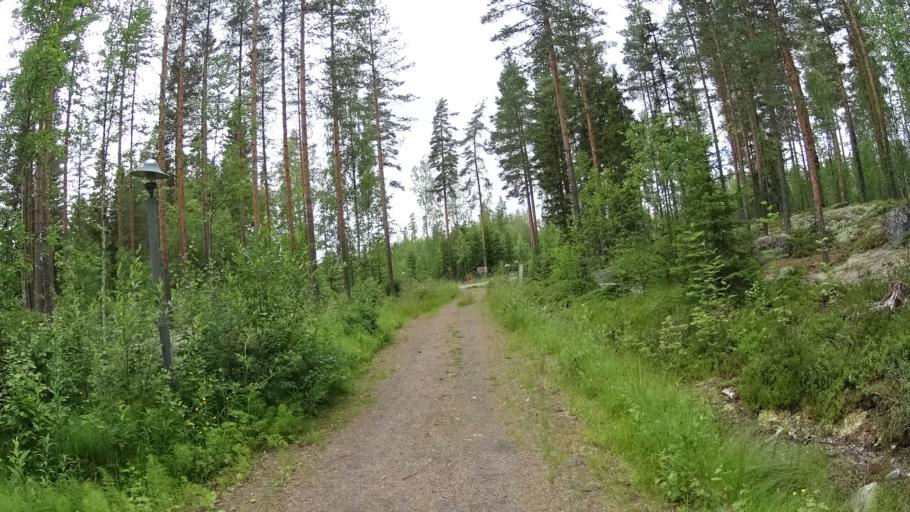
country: FI
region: Southern Ostrobothnia
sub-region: Kuusiokunnat
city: AEhtaeri
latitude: 62.5306
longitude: 24.1909
